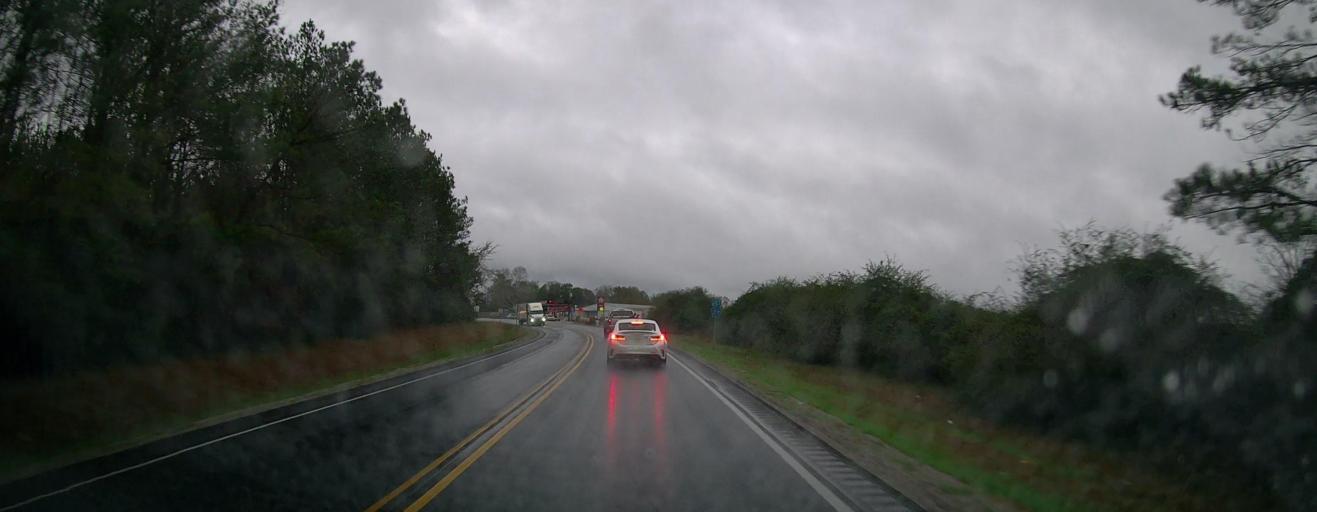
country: US
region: Alabama
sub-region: Chilton County
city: Clanton
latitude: 32.6260
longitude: -86.7379
